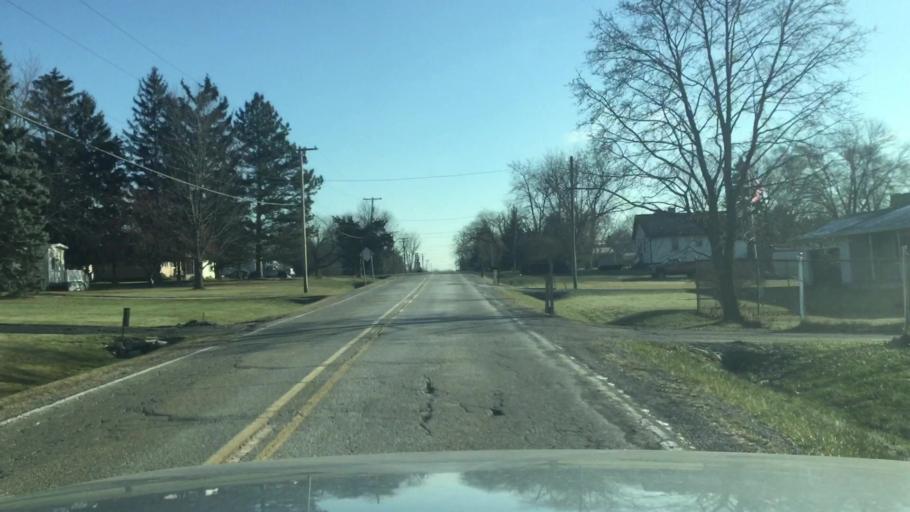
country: US
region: Michigan
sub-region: Genesee County
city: Grand Blanc
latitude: 42.9353
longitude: -83.6605
